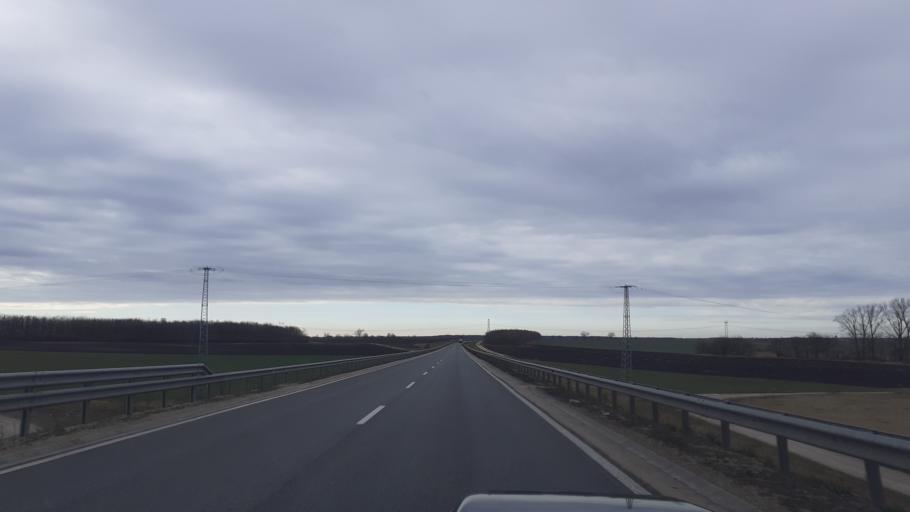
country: HU
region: Fejer
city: Perkata
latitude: 47.0654
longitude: 18.7657
